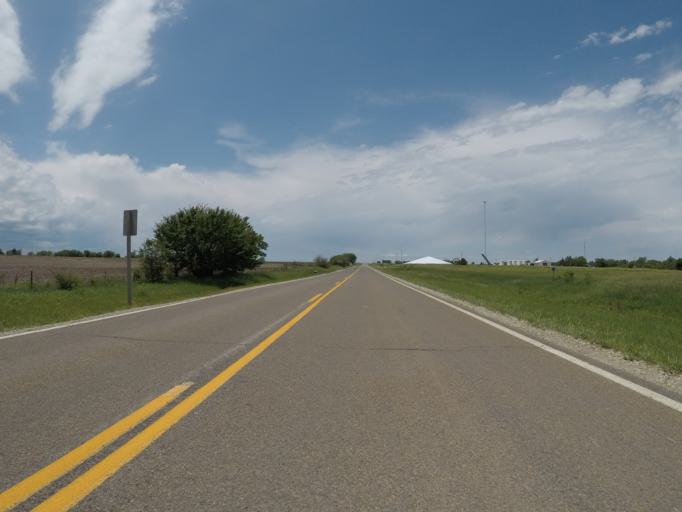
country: US
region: Kansas
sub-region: Morris County
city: Council Grove
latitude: 38.8551
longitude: -96.4872
